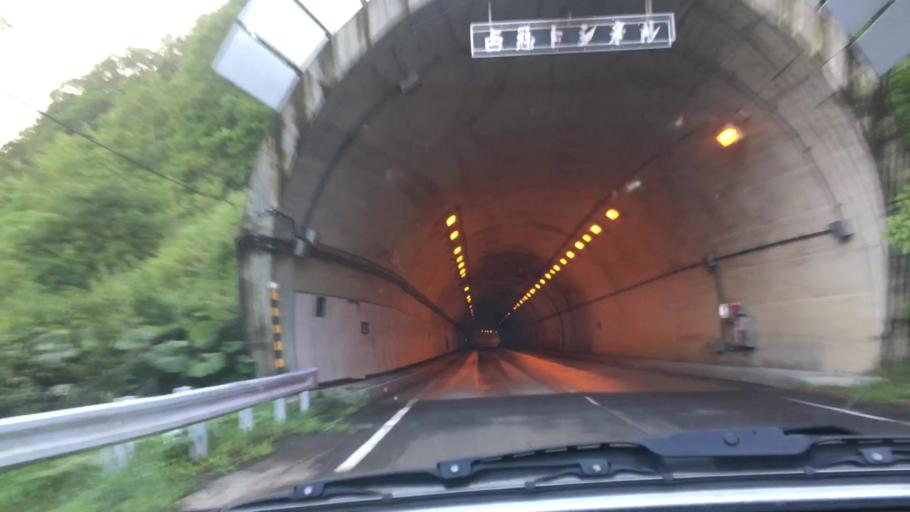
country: JP
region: Hokkaido
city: Shimo-furano
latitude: 43.0437
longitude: 142.4679
